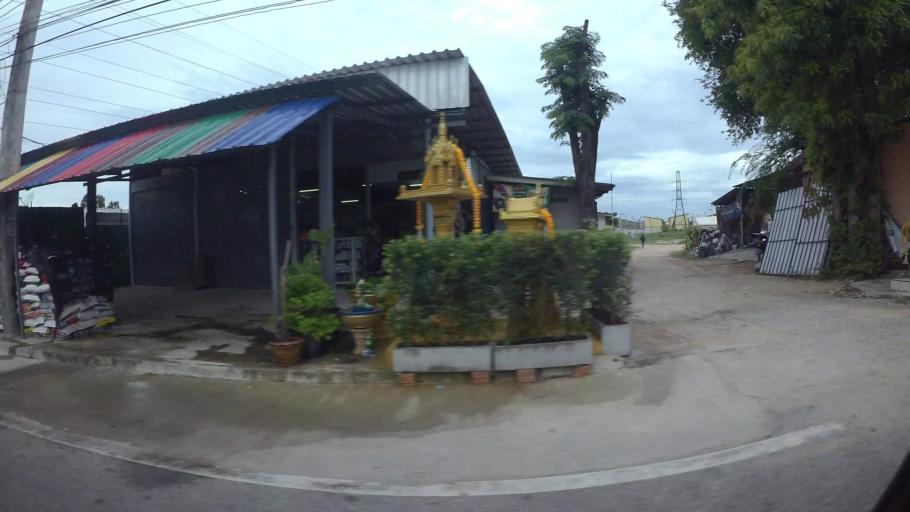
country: TH
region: Chon Buri
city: Si Racha
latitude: 13.1374
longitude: 100.9393
